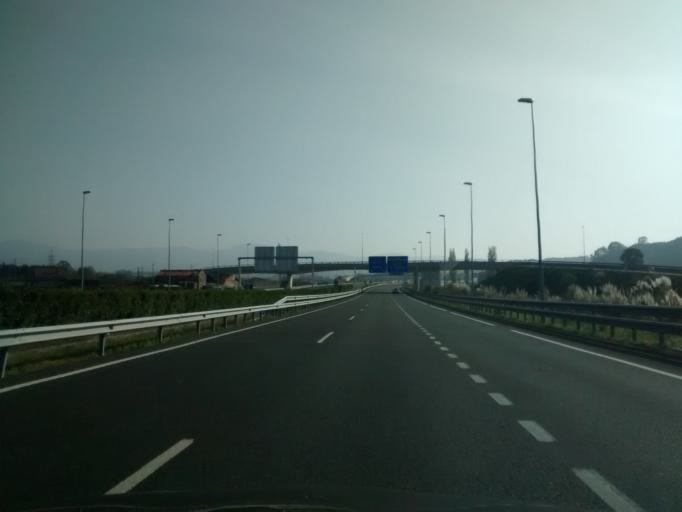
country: ES
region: Cantabria
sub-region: Provincia de Cantabria
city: Camargo
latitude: 43.4291
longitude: -3.8740
